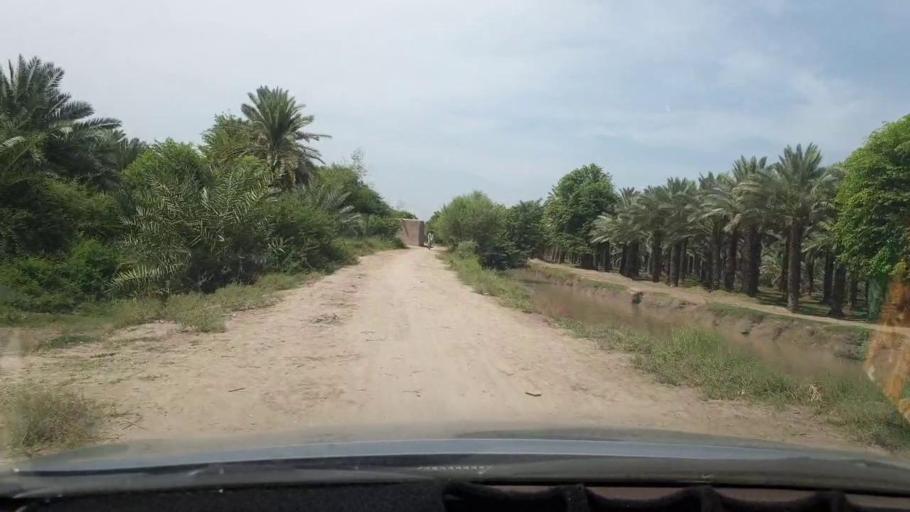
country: PK
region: Sindh
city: Khairpur
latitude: 27.4980
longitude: 68.7483
